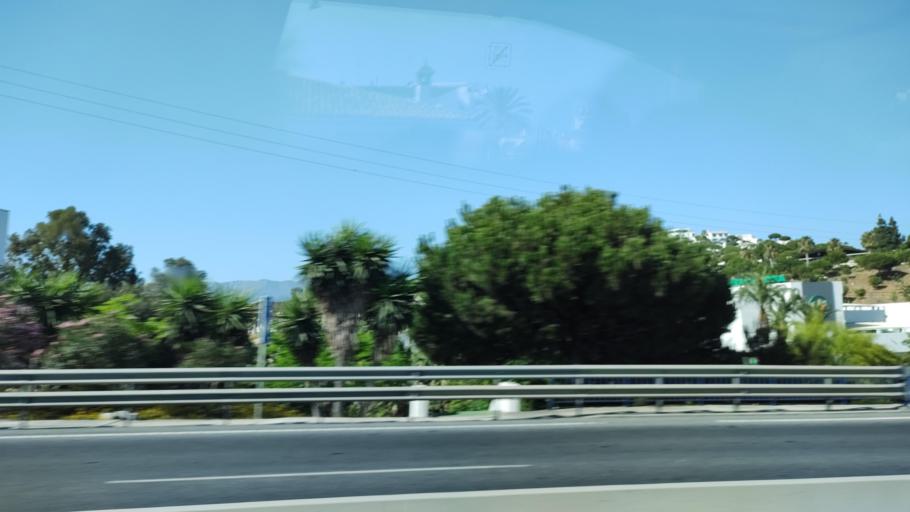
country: ES
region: Andalusia
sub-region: Provincia de Malaga
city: Fuengirola
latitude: 36.5062
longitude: -4.6777
